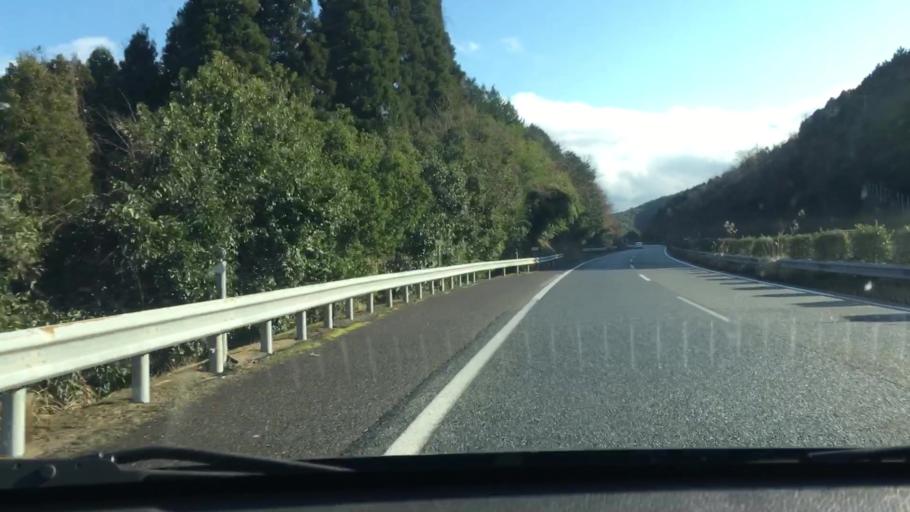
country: JP
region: Kumamoto
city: Hitoyoshi
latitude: 32.1753
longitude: 130.7895
